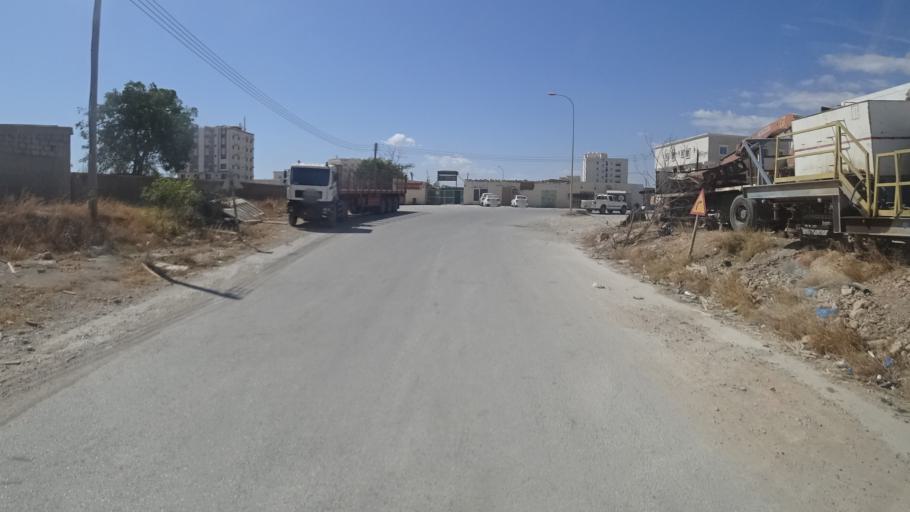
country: OM
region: Zufar
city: Salalah
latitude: 17.0235
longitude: 54.0368
